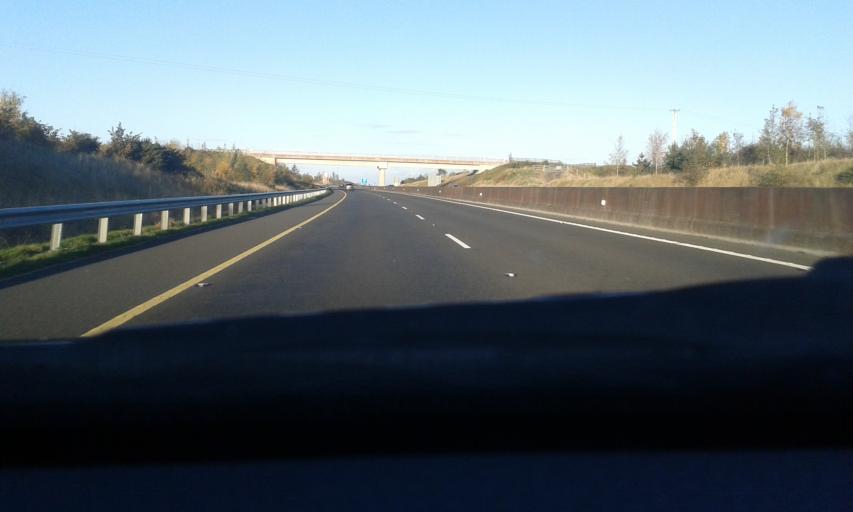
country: IE
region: Leinster
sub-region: Laois
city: Rathdowney
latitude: 52.7968
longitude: -7.5122
